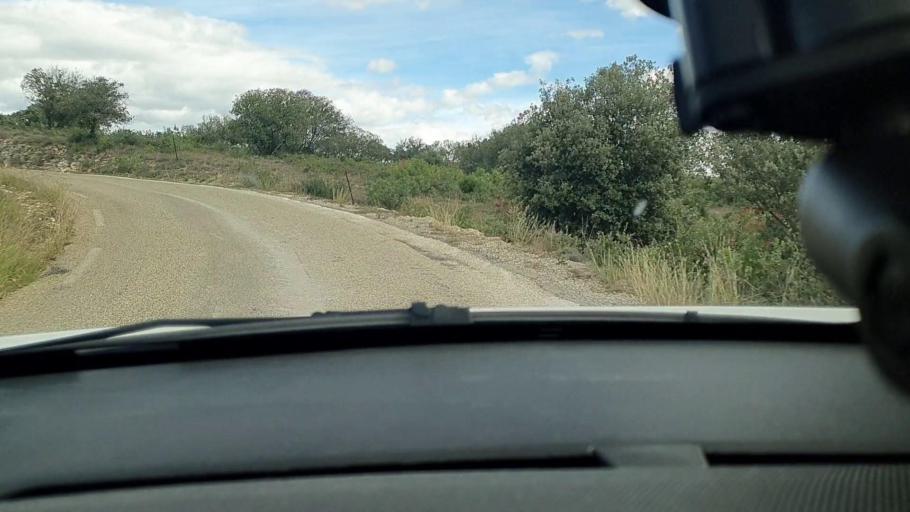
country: FR
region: Languedoc-Roussillon
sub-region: Departement du Gard
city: Salindres
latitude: 44.1684
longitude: 4.2575
